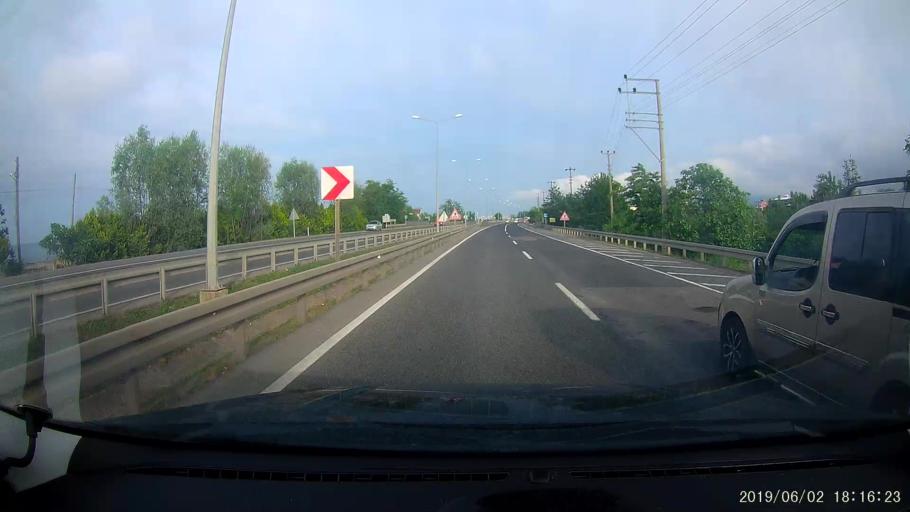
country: TR
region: Ordu
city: Unieh
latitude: 41.1009
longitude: 37.3977
